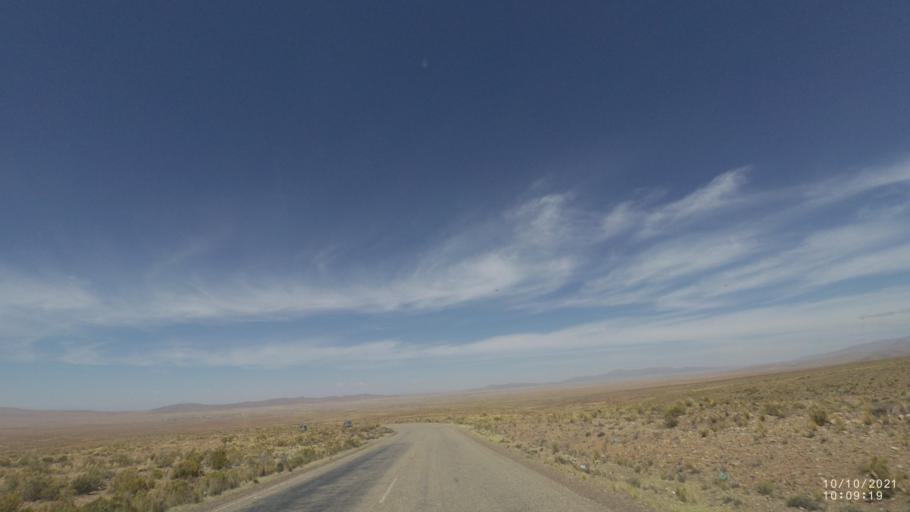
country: BO
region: La Paz
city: Eucaliptus
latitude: -17.3991
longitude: -67.4875
